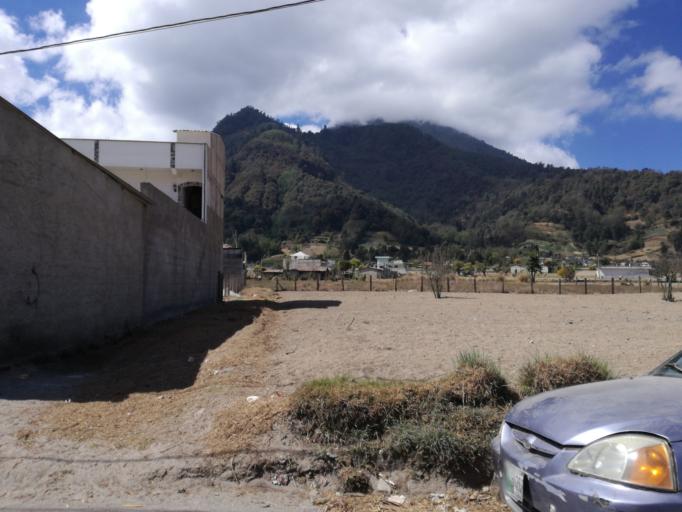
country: GT
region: Quetzaltenango
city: Almolonga
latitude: 14.7888
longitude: -91.5395
